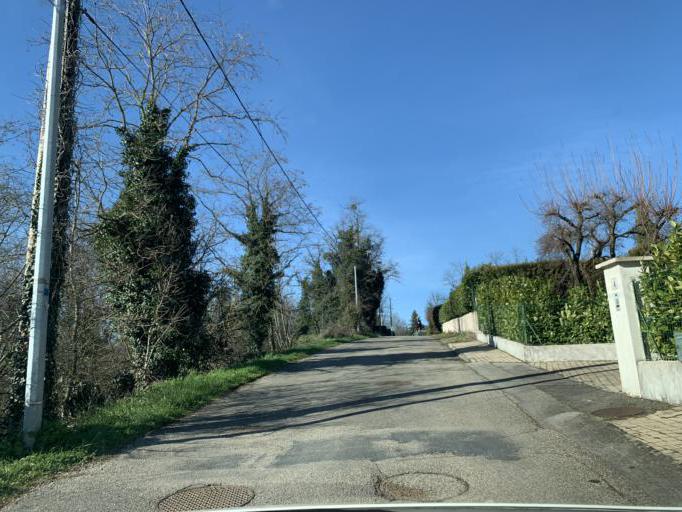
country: FR
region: Rhone-Alpes
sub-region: Departement du Rhone
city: Rillieux-la-Pape
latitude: 45.8176
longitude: 4.9275
